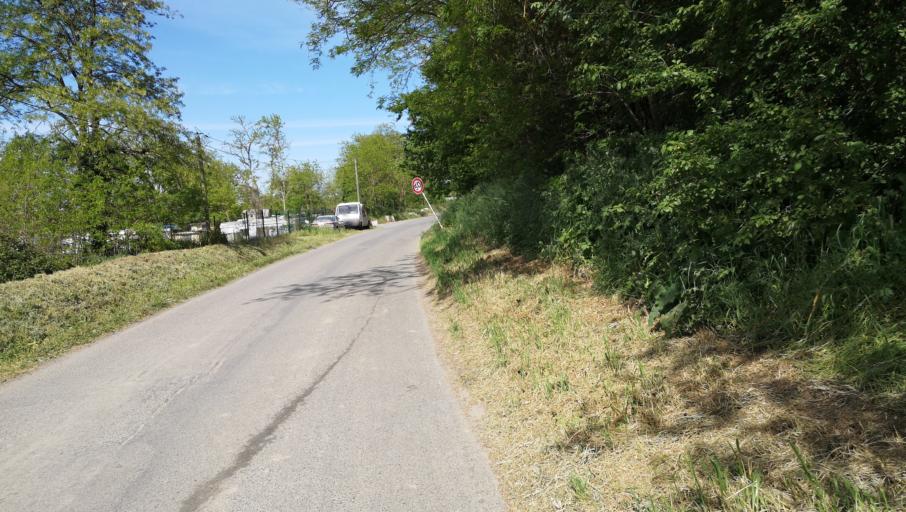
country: FR
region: Midi-Pyrenees
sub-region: Departement de la Haute-Garonne
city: Blagnac
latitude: 43.6477
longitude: 1.3979
